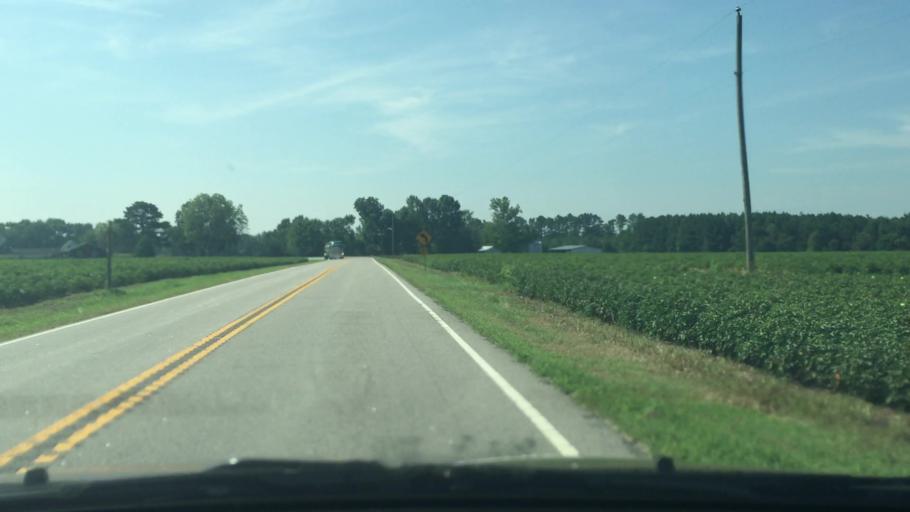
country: US
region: Virginia
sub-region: Southampton County
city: Courtland
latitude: 36.8455
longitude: -77.1326
